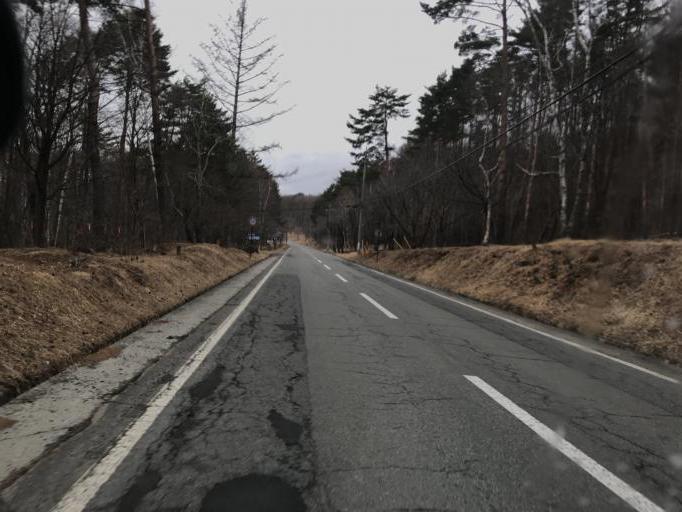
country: JP
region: Nagano
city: Chino
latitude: 35.9025
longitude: 138.3165
